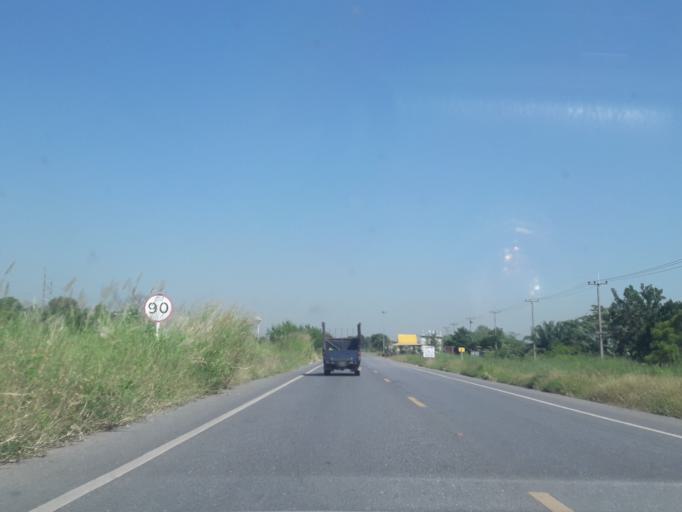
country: TH
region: Sara Buri
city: Nong Khae
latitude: 14.2637
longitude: 100.8234
